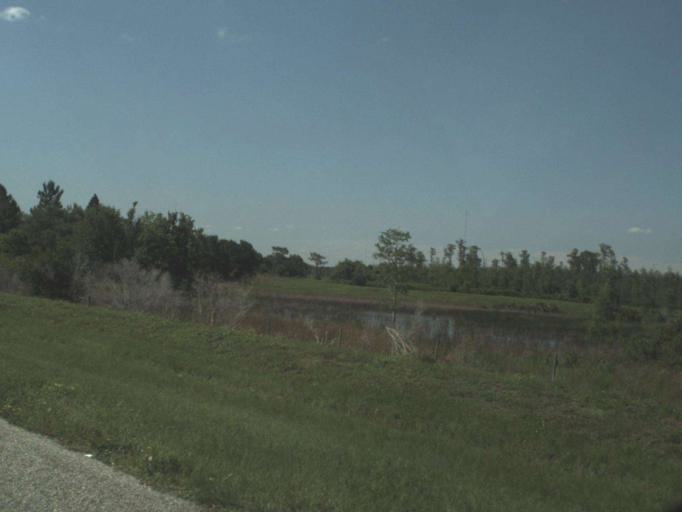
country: US
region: Florida
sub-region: Orange County
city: Wedgefield
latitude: 28.5138
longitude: -81.0619
